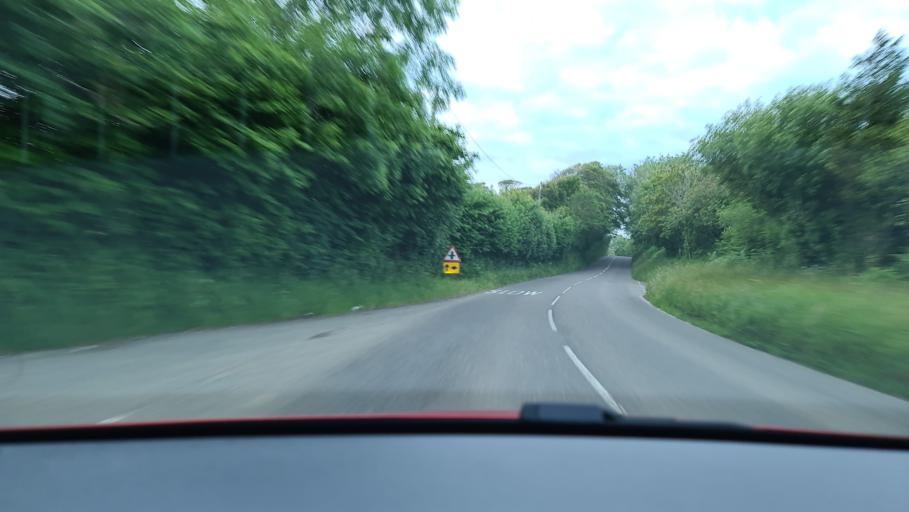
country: GB
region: England
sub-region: Cornwall
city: Liskeard
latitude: 50.4202
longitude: -4.4348
